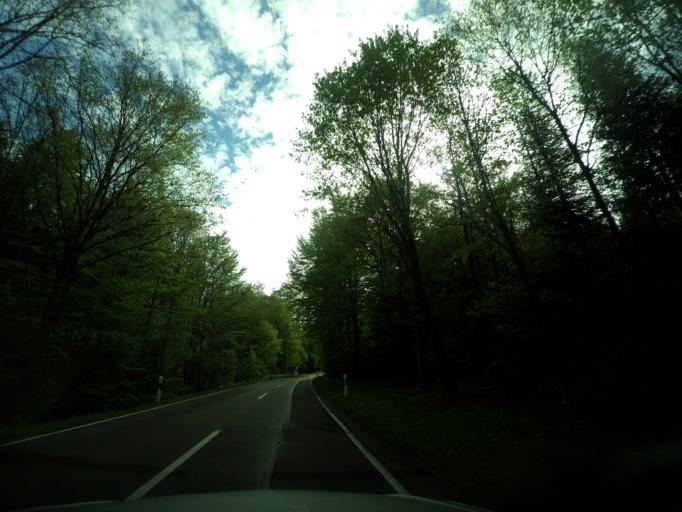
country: DE
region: Baden-Wuerttemberg
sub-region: Regierungsbezirk Stuttgart
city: Gschwend
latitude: 48.9484
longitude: 9.7247
